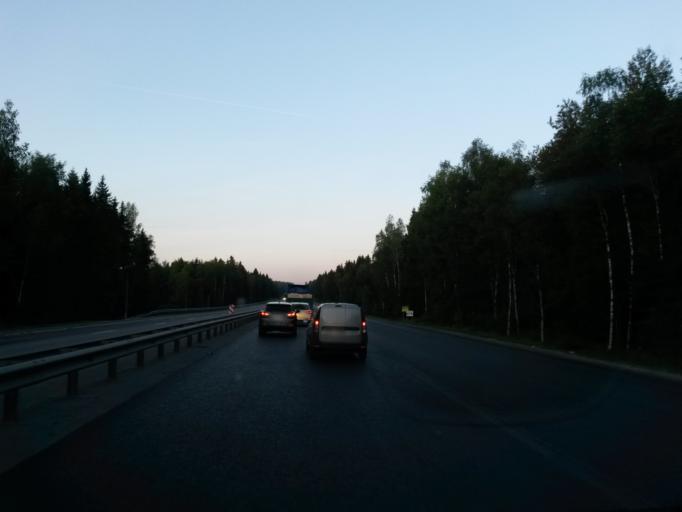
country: RU
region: Moskovskaya
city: Svatkovo
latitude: 56.3158
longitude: 38.2465
